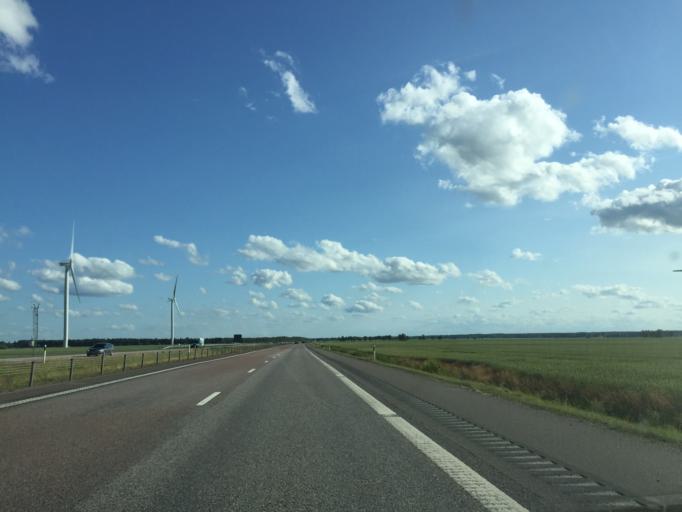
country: SE
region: OErebro
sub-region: Kumla Kommun
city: Kumla
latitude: 59.1936
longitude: 15.1249
